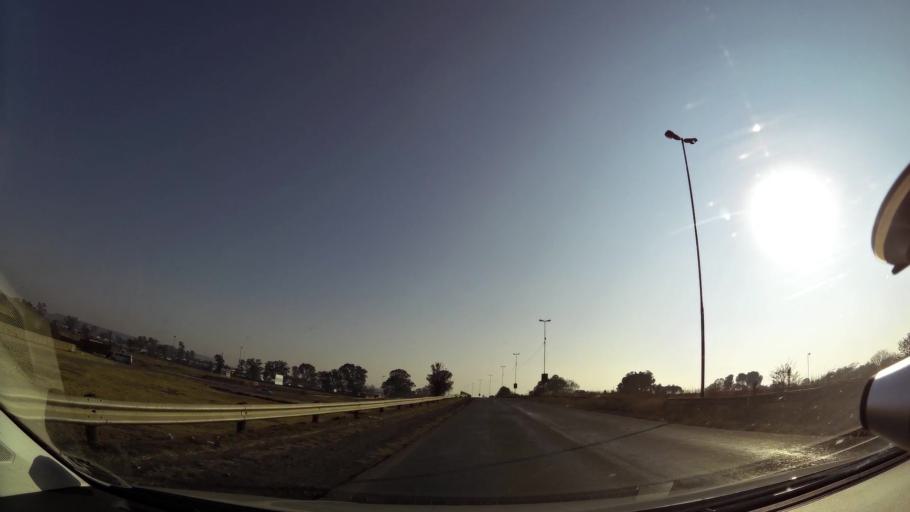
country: ZA
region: Orange Free State
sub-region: Mangaung Metropolitan Municipality
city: Bloemfontein
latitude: -29.1371
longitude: 26.2670
